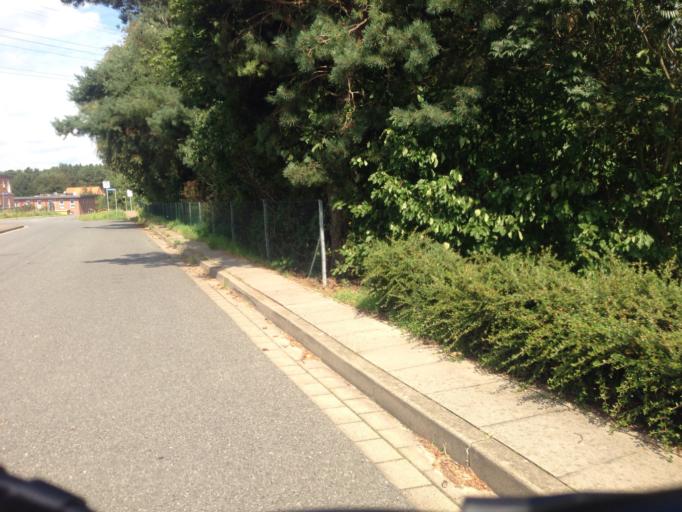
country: DE
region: Lower Saxony
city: Adendorf
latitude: 53.2920
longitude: 10.4288
